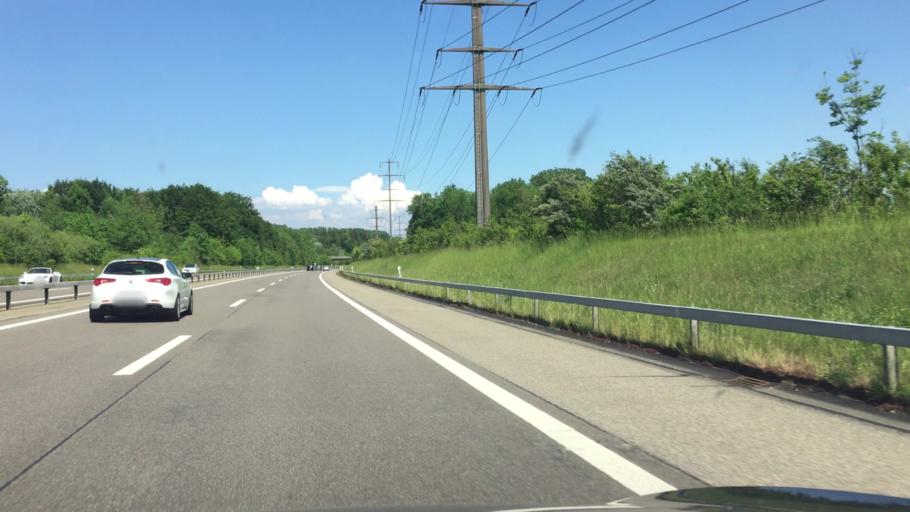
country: CH
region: Thurgau
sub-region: Frauenfeld District
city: Pfyn
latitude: 47.5824
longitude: 8.9306
